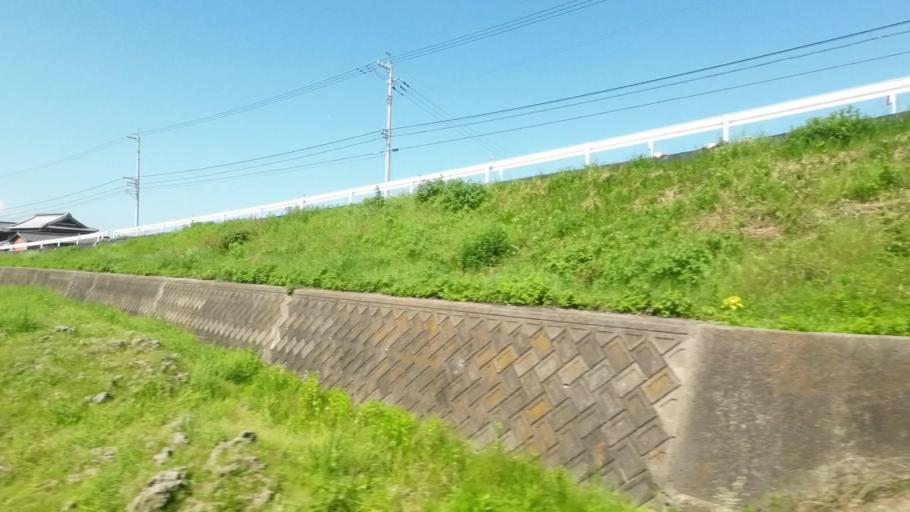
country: JP
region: Kagawa
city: Kan'onjicho
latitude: 34.1089
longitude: 133.6497
